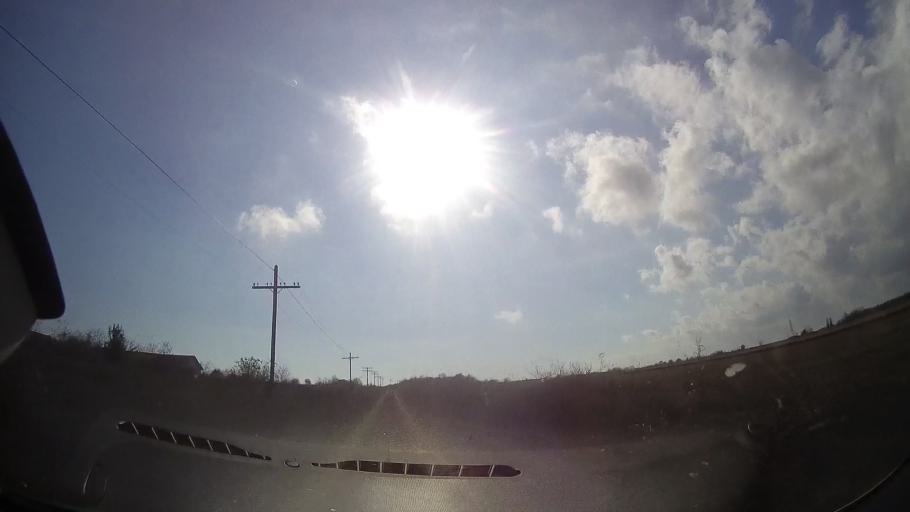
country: RO
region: Constanta
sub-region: Comuna Tuzla
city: Tuzla
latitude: 43.9917
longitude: 28.6451
